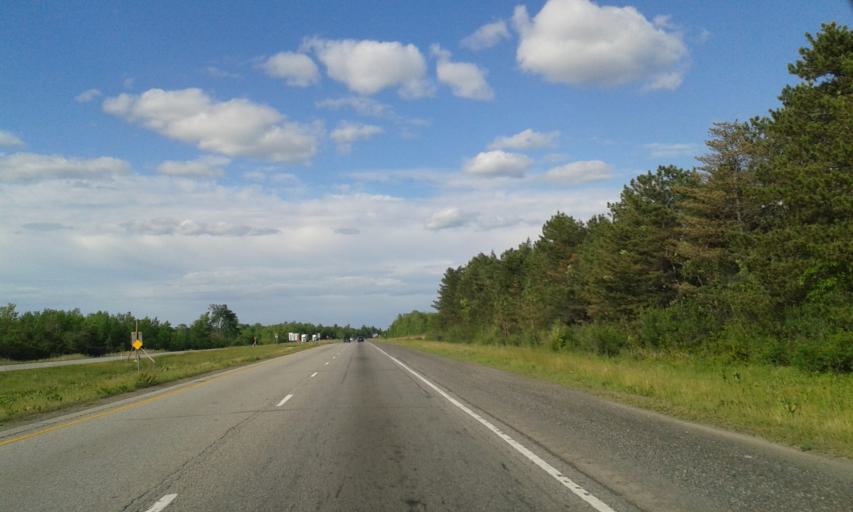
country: CA
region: Ontario
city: Prescott
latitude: 44.7051
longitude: -75.5635
